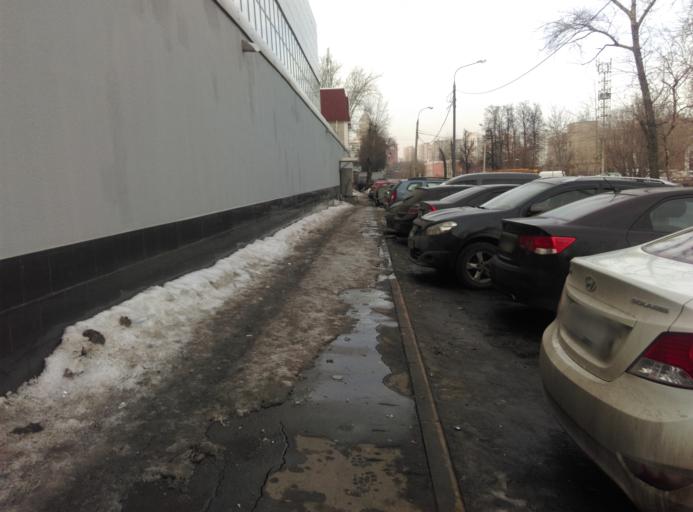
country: RU
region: Moskovskaya
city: Bol'shaya Setun'
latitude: 55.7118
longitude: 37.4212
